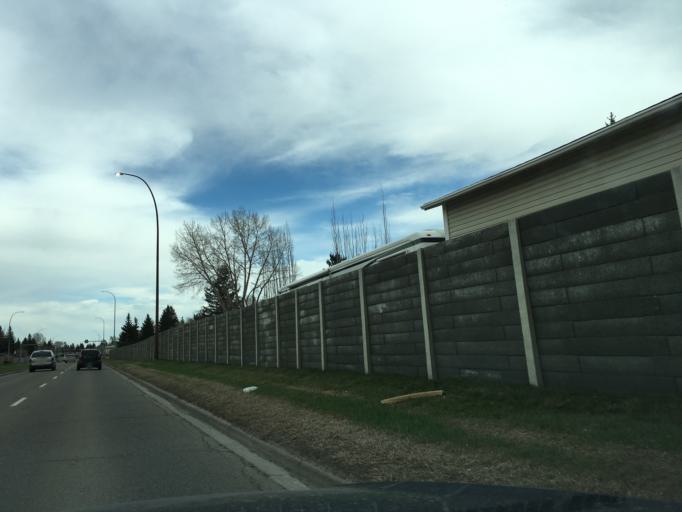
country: CA
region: Alberta
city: Calgary
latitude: 50.9640
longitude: -114.0554
